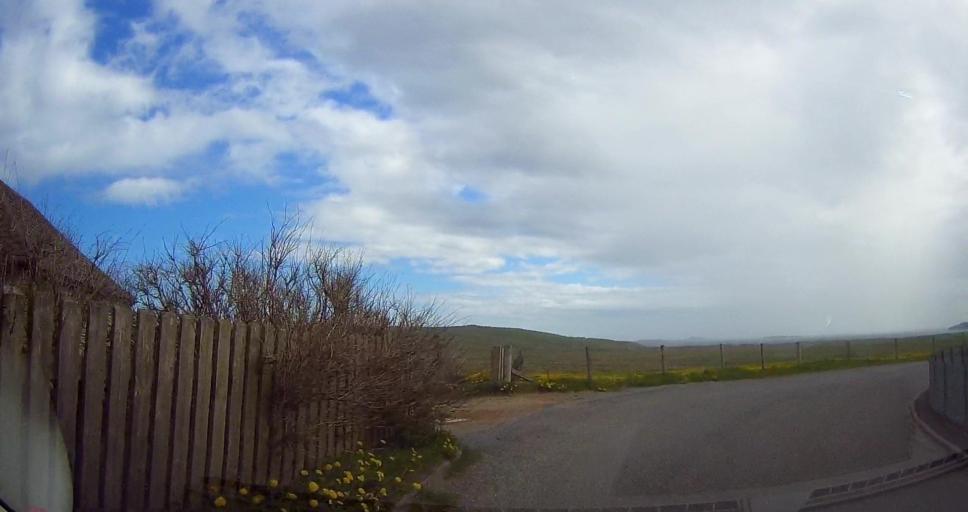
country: GB
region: Scotland
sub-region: Shetland Islands
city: Sandwick
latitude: 59.9129
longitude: -1.3238
